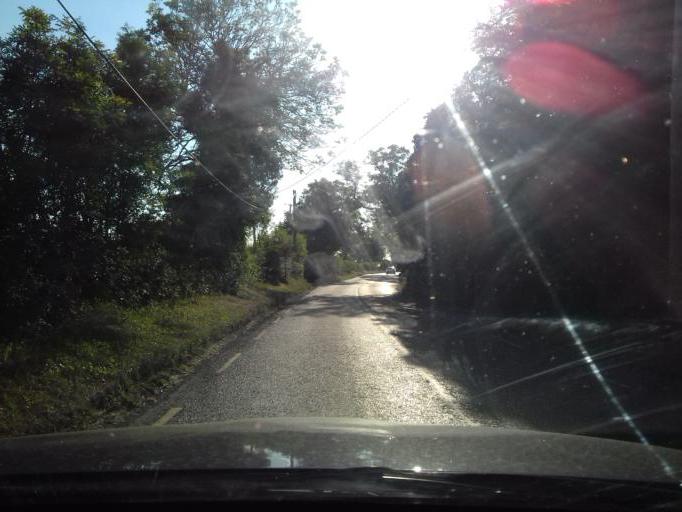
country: IE
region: Leinster
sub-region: An Mhi
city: Ashbourne
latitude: 53.5109
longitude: -6.3496
